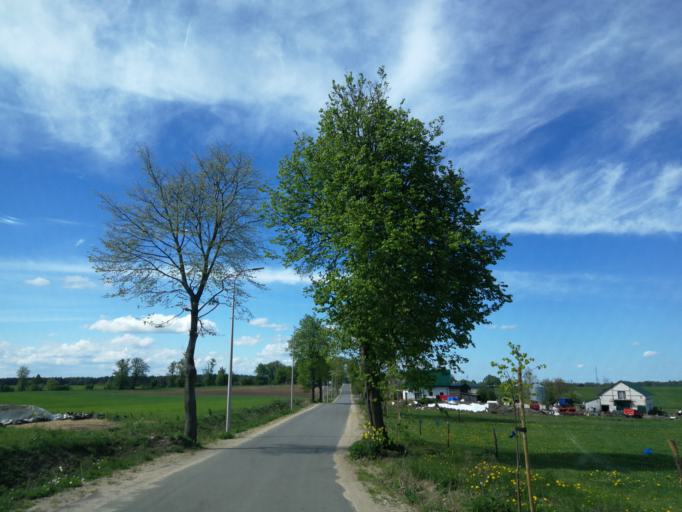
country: PL
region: Warmian-Masurian Voivodeship
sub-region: Powiat ilawski
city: Ilawa
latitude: 53.6102
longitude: 19.6745
